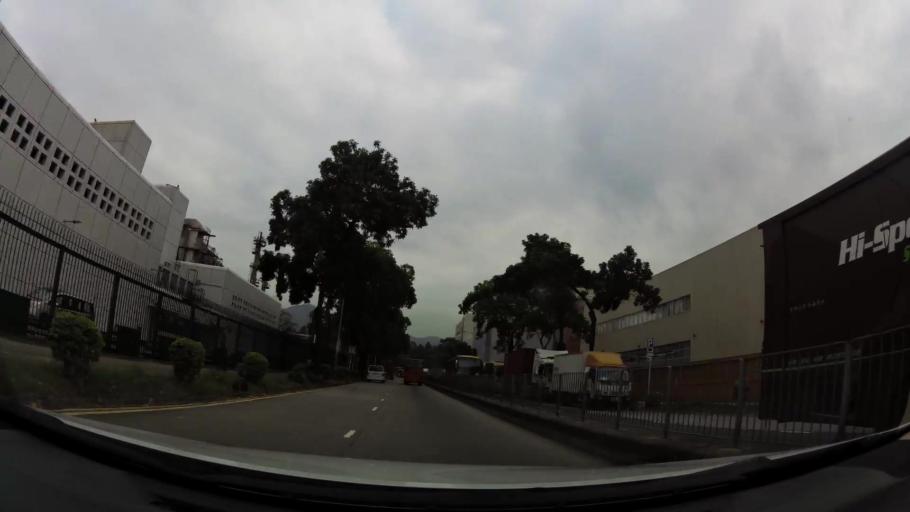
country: HK
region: Tai Po
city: Tai Po
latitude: 22.4554
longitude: 114.1812
